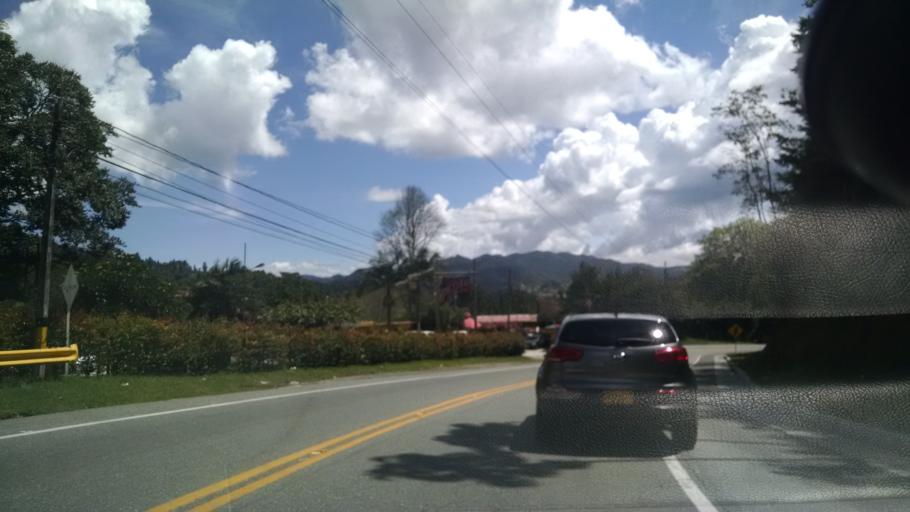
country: CO
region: Antioquia
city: El Retiro
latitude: 6.1219
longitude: -75.5008
